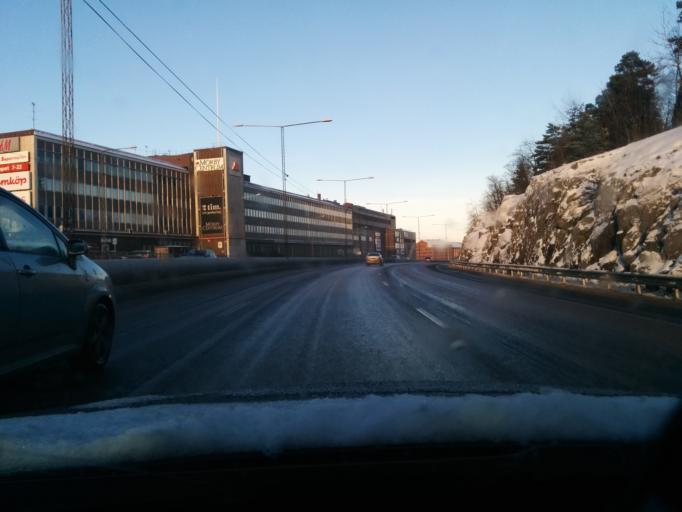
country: SE
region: Stockholm
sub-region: Norrtalje Kommun
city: Bergshamra
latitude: 59.3966
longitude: 18.0385
